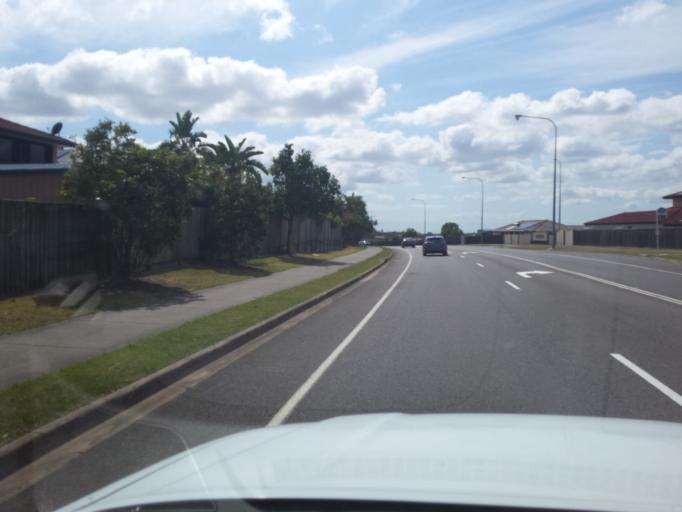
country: AU
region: Queensland
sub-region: Moreton Bay
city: Ferny Hills
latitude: -27.3822
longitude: 152.9562
